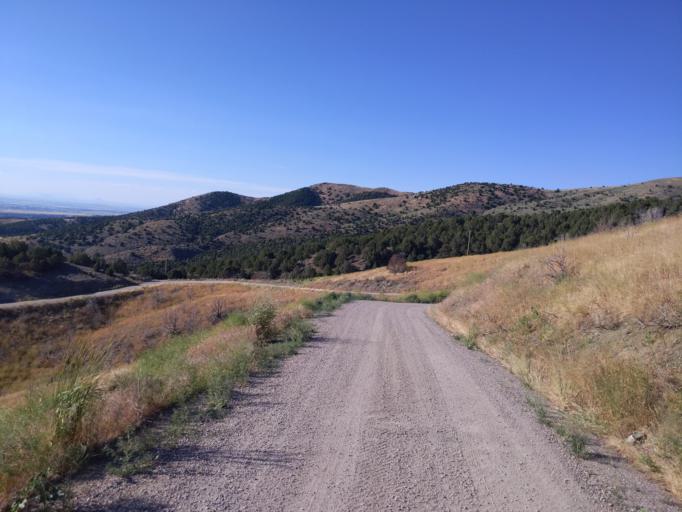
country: US
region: Idaho
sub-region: Bannock County
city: Pocatello
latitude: 42.8505
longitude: -112.3777
